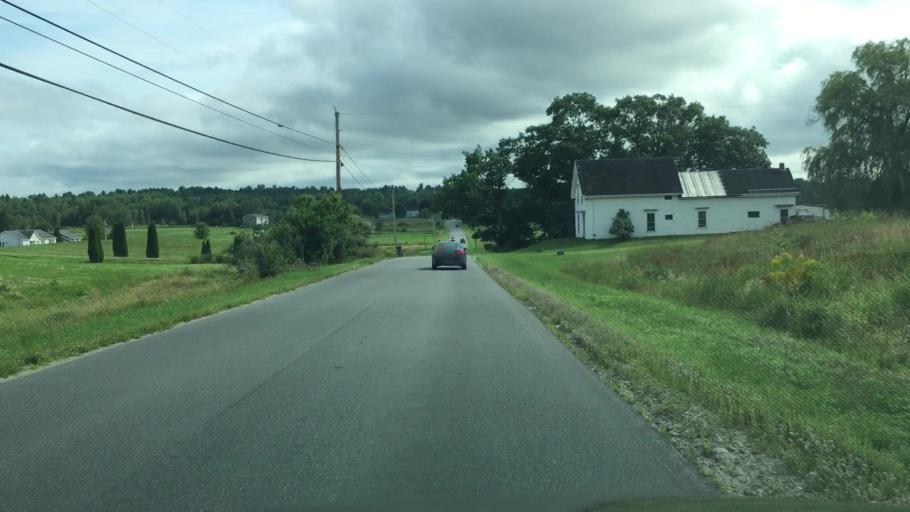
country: US
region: Maine
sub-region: Waldo County
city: Winterport
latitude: 44.6766
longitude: -68.8679
